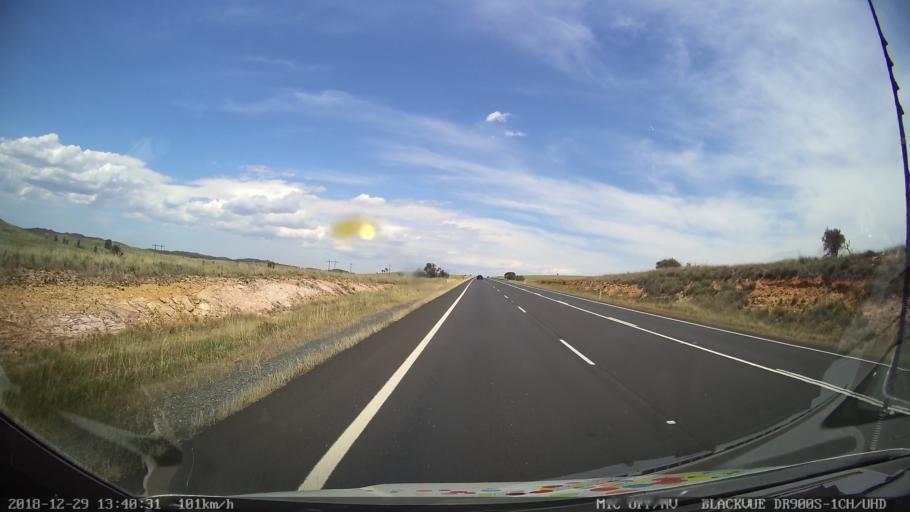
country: AU
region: New South Wales
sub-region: Cooma-Monaro
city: Cooma
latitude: -36.0282
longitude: 149.1526
